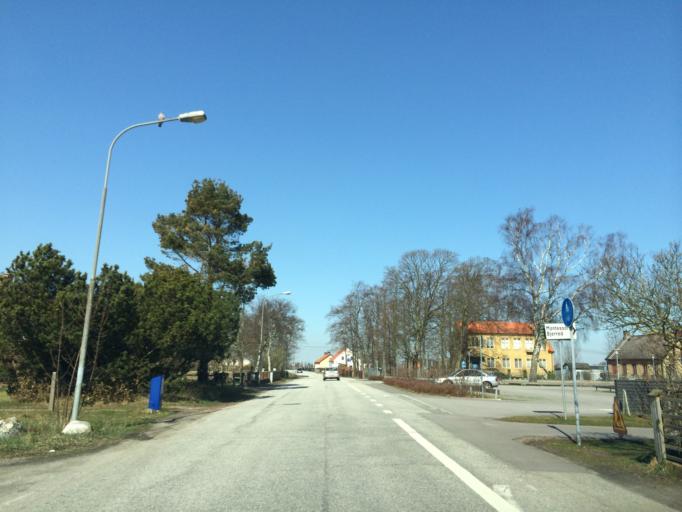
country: SE
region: Skane
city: Bjarred
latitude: 55.7372
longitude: 13.0316
